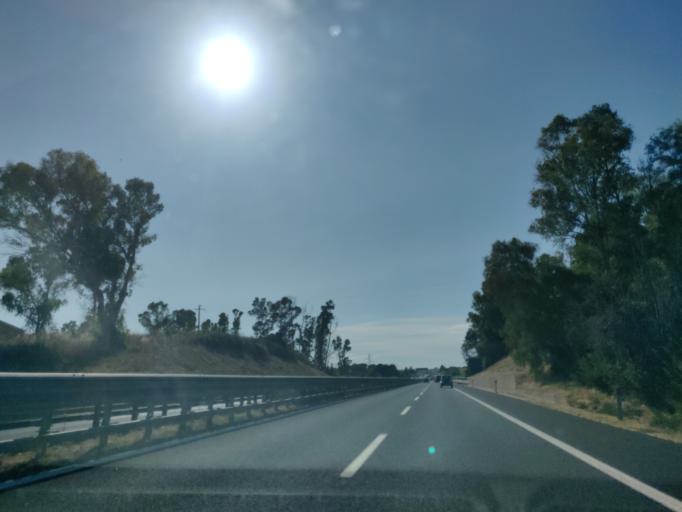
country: IT
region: Latium
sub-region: Citta metropolitana di Roma Capitale
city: Valcanneto
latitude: 41.9301
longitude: 12.1845
